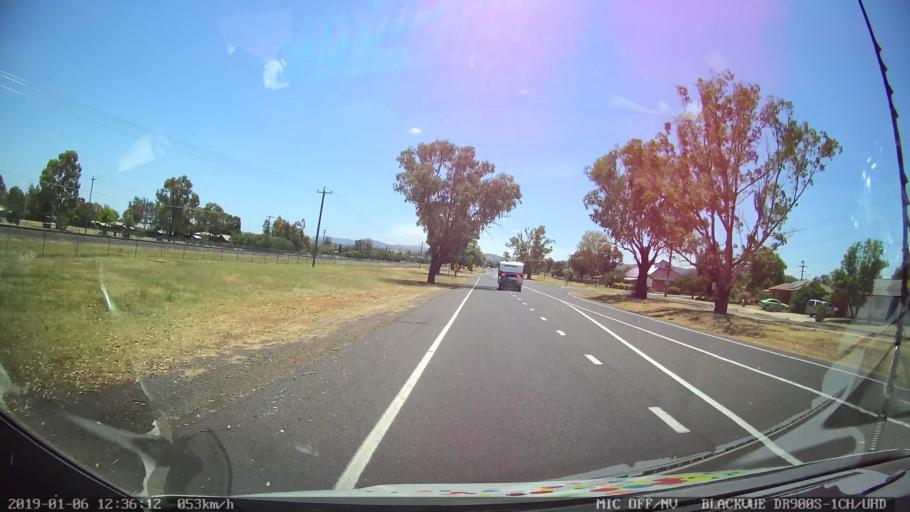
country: AU
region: New South Wales
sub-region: Tamworth Municipality
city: South Tamworth
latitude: -31.1129
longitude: 150.8957
